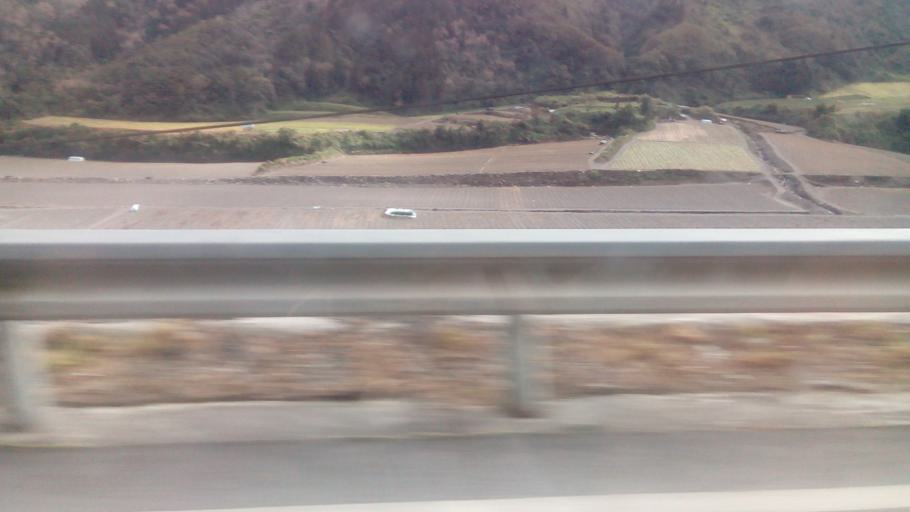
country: TW
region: Taiwan
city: Daxi
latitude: 24.4542
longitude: 121.3919
